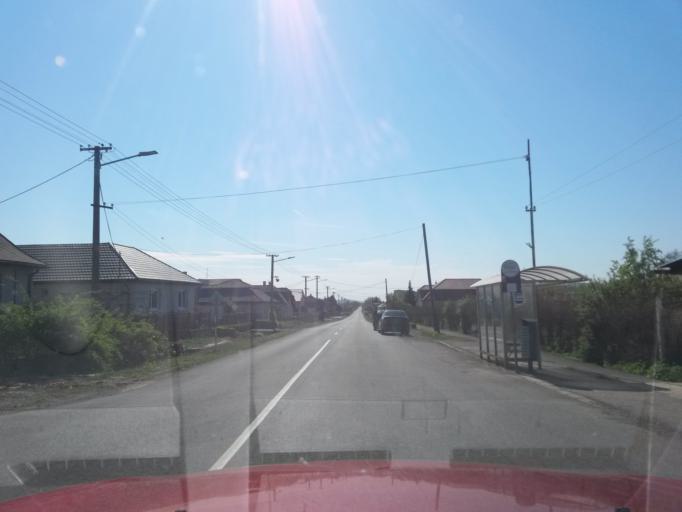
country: SK
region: Kosicky
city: Trebisov
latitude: 48.5501
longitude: 21.5578
